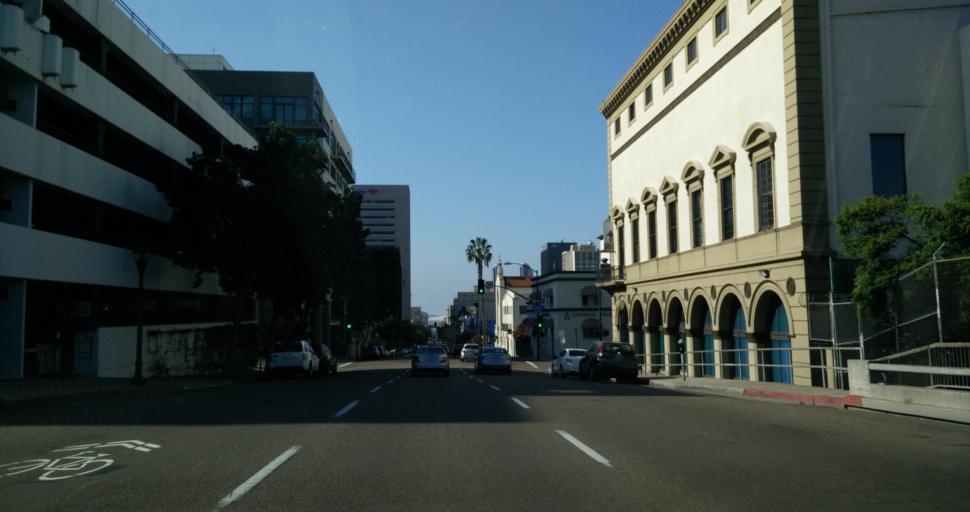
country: US
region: California
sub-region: San Diego County
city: San Diego
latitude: 32.7226
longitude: -117.1612
